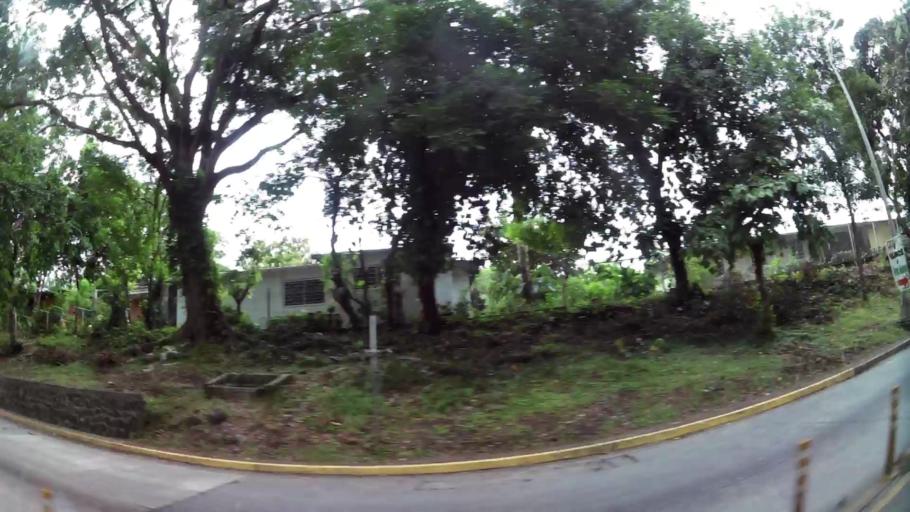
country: PA
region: Panama
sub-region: Distrito de Panama
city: Ancon
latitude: 8.9488
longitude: -79.5559
